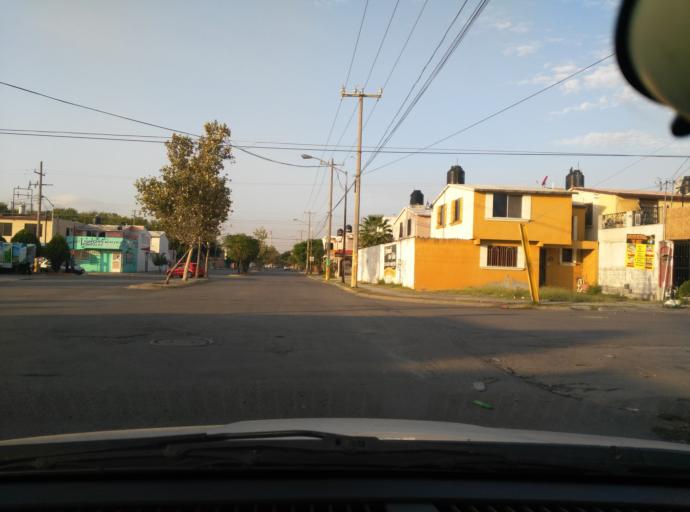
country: MX
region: Nuevo Leon
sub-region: San Nicolas de los Garza
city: San Nicolas de los Garza
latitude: 25.7643
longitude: -100.2499
